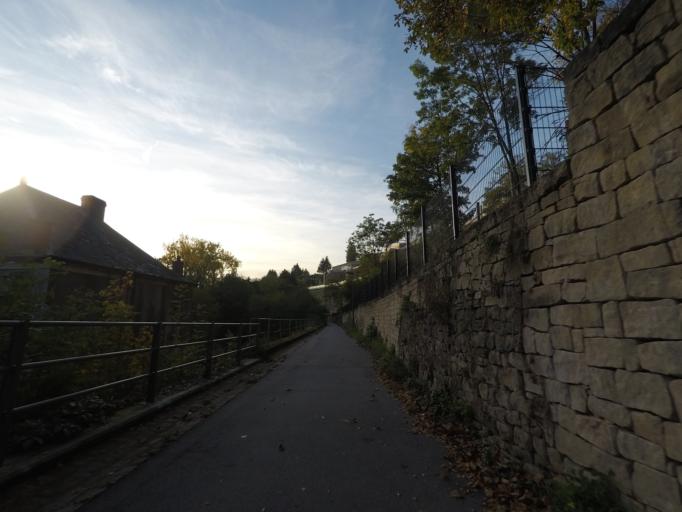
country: LU
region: Luxembourg
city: Kirchberg
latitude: 49.6096
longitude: 6.1463
